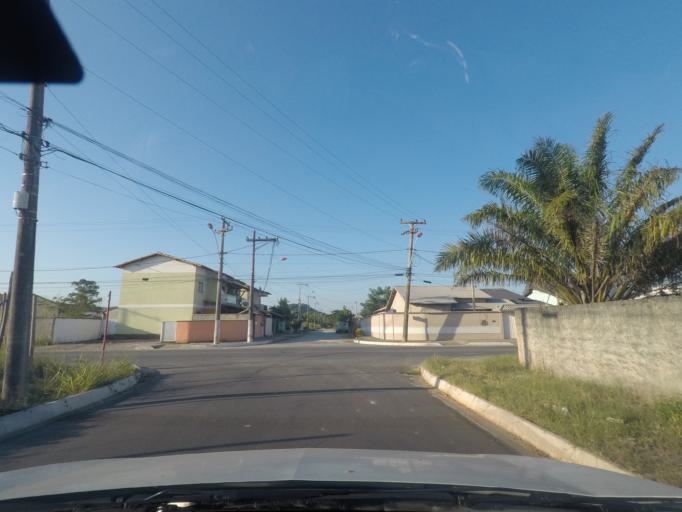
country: BR
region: Rio de Janeiro
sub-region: Marica
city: Marica
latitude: -22.9567
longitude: -42.9334
